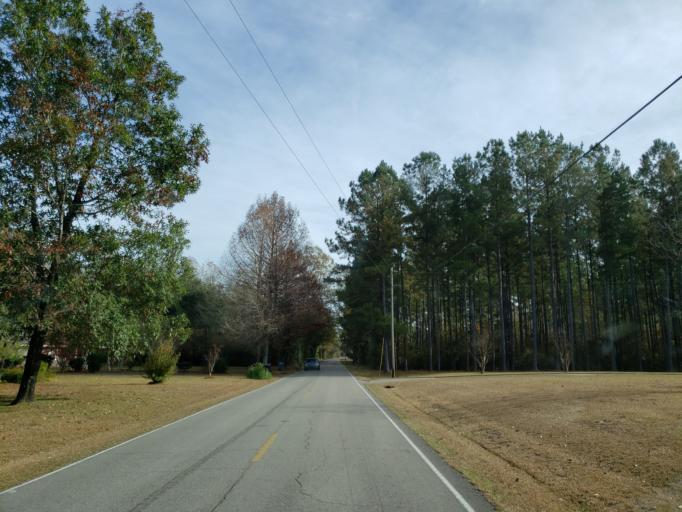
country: US
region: Mississippi
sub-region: Forrest County
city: Rawls Springs
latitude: 31.3932
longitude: -89.3842
